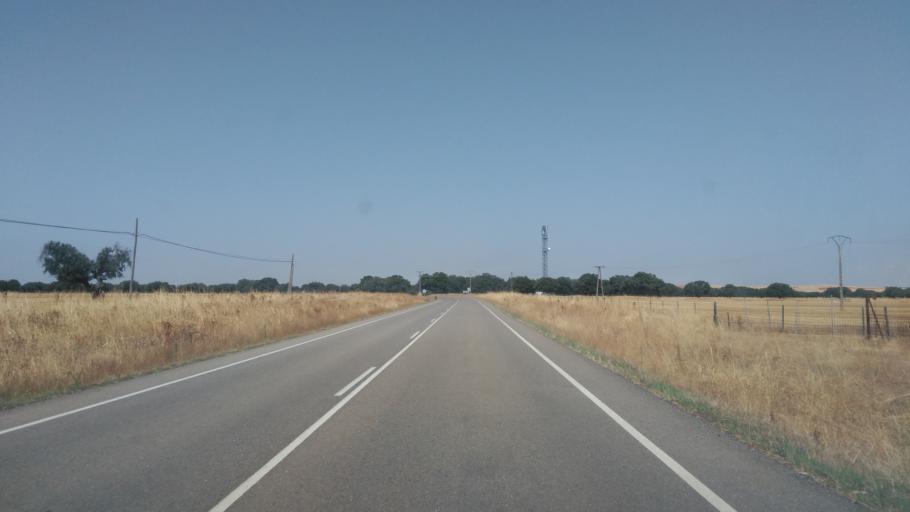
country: ES
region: Castille and Leon
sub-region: Provincia de Salamanca
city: Abusejo
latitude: 40.7214
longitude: -6.1504
